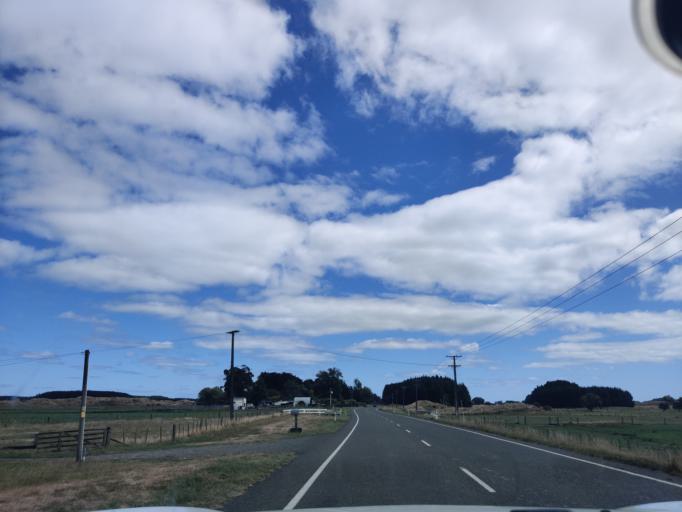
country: NZ
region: Manawatu-Wanganui
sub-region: Horowhenua District
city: Foxton
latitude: -40.4052
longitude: 175.3716
